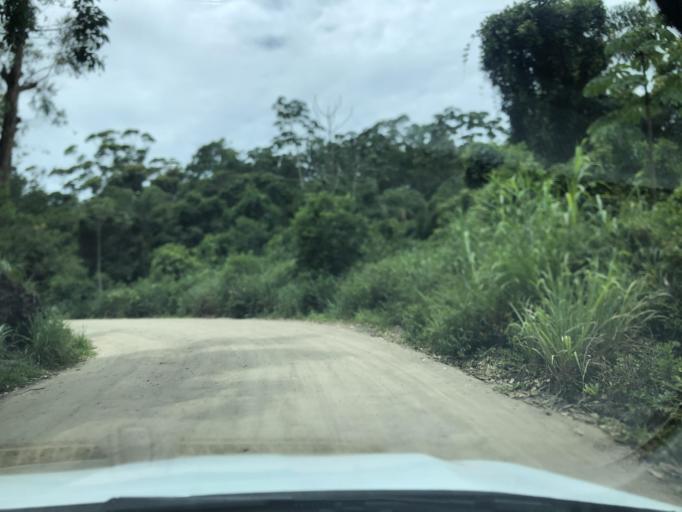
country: BR
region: Santa Catarina
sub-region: Florianopolis
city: Lagoa
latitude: -27.5238
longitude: -48.4211
